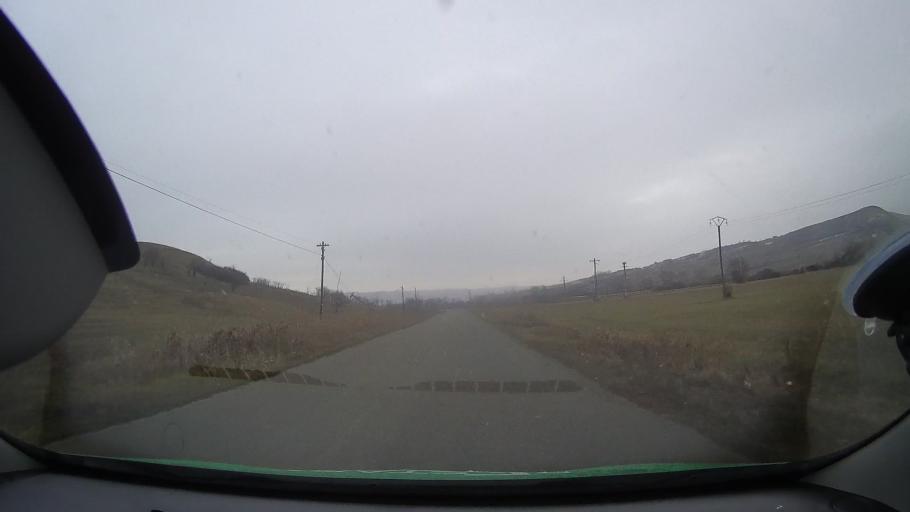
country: RO
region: Alba
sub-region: Comuna Farau
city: Farau
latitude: 46.3343
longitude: 23.9770
